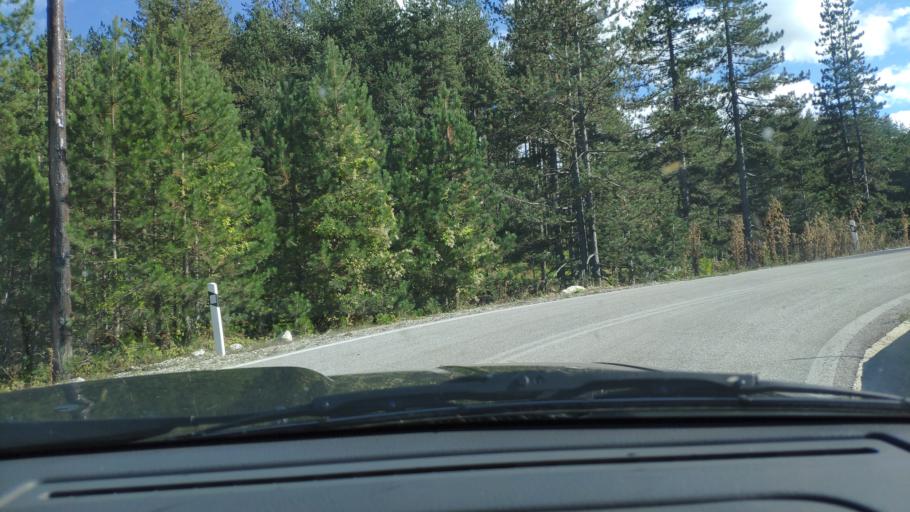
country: AL
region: Korce
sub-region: Rrethi i Devollit
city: Miras
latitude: 40.4091
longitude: 20.8777
